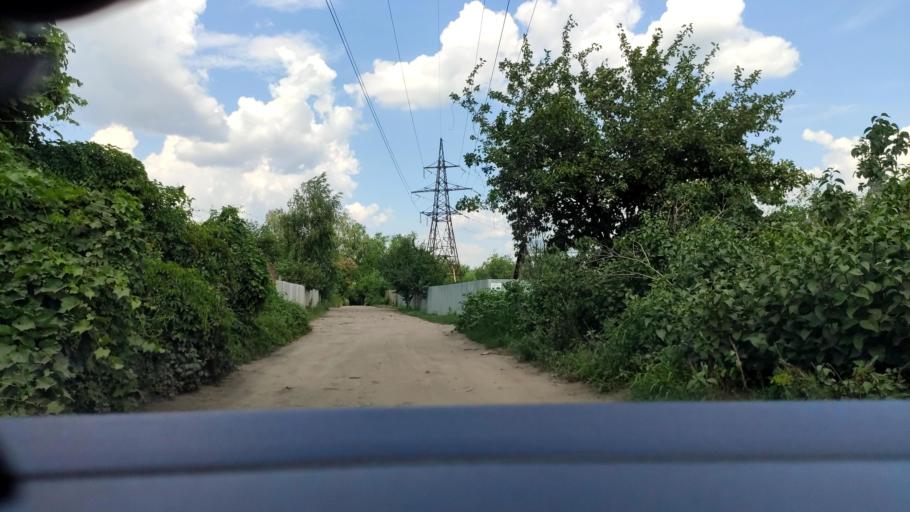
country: RU
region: Voronezj
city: Maslovka
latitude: 51.6052
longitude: 39.2860
